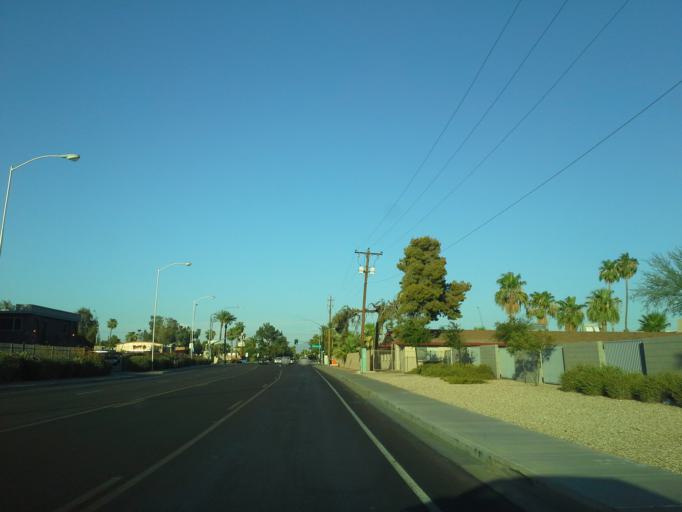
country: US
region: Arizona
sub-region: Maricopa County
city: Mesa
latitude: 33.4351
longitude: -111.8417
